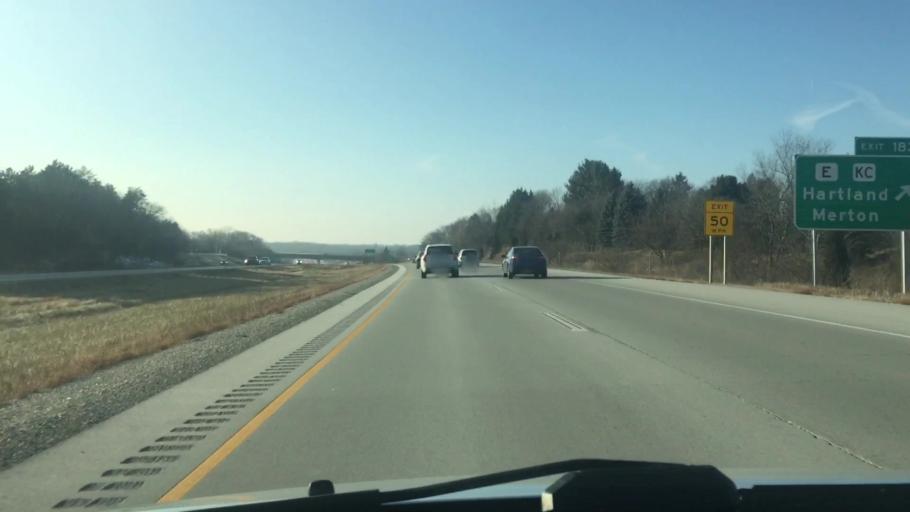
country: US
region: Wisconsin
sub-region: Waukesha County
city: Hartland
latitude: 43.1095
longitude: -88.3263
